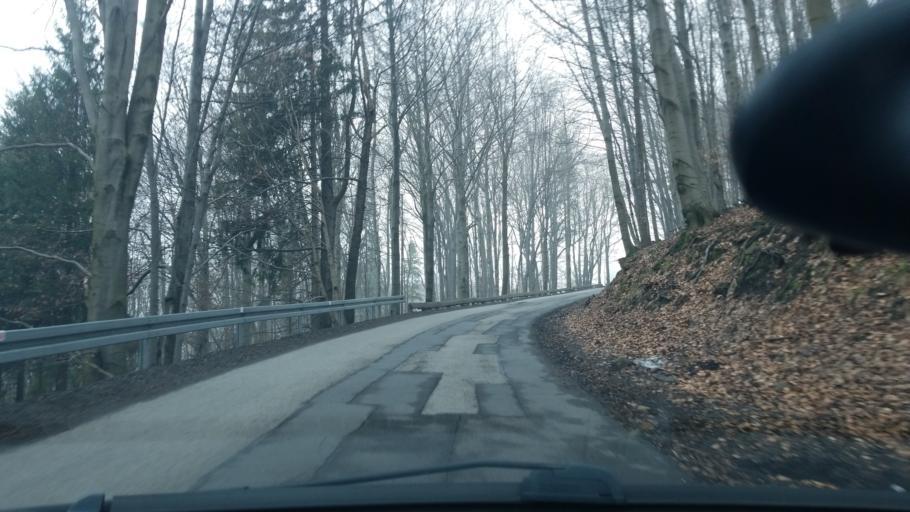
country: PL
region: Silesian Voivodeship
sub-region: Powiat cieszynski
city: Ustron
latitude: 49.7179
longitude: 18.8426
